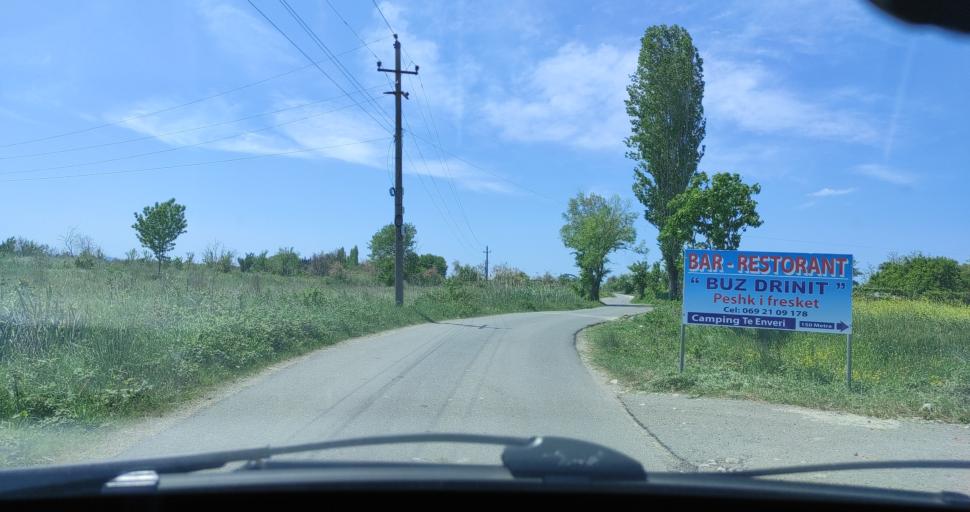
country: AL
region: Lezhe
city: Lezhe
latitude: 41.7547
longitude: 19.6100
